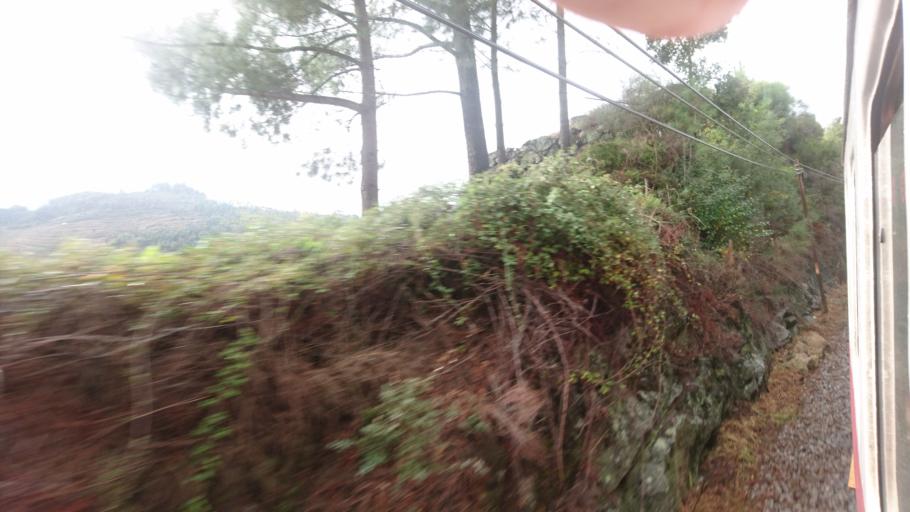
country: PT
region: Viseu
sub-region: Cinfaes
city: Cinfaes
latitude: 41.0940
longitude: -8.0790
